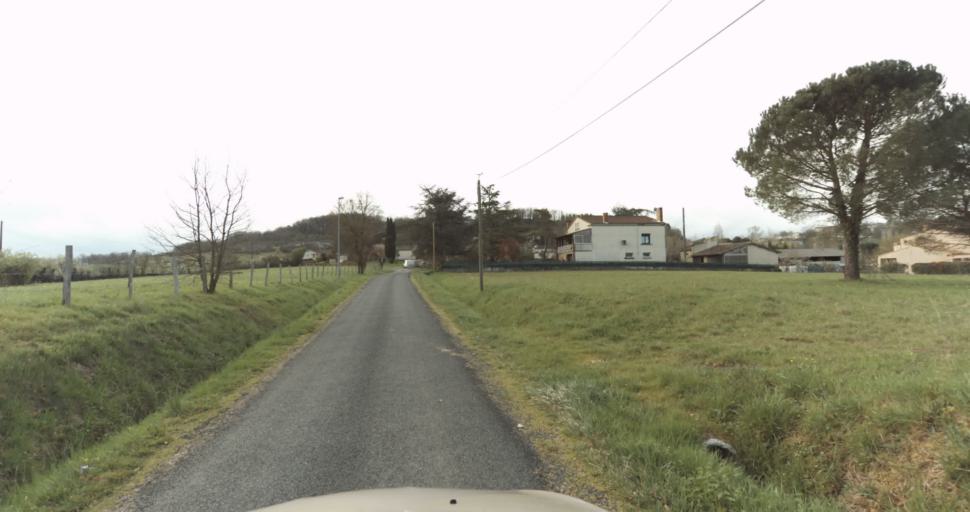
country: FR
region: Midi-Pyrenees
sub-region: Departement du Tarn
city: Puygouzon
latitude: 43.9078
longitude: 2.1746
